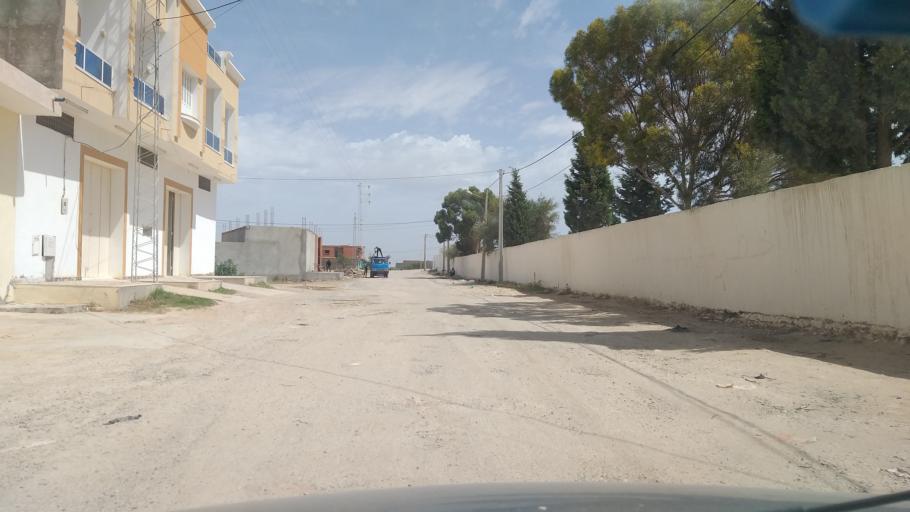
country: TN
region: Al Mahdiyah
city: El Jem
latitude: 35.3100
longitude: 10.7038
